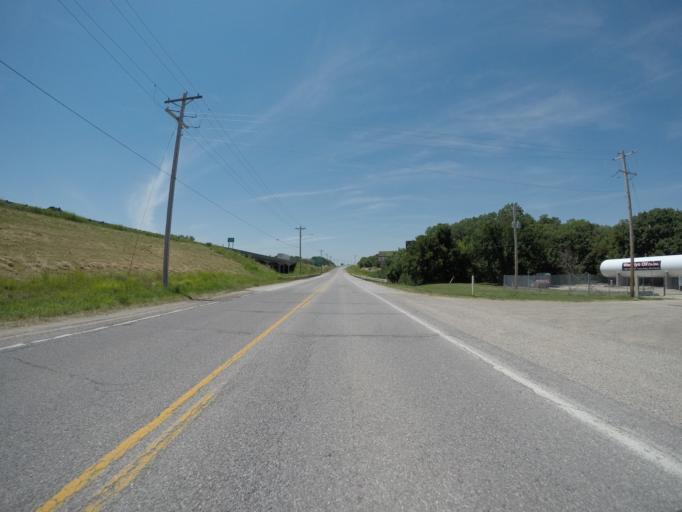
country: US
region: Kansas
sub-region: Geary County
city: Grandview Plaza
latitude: 39.0305
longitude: -96.7852
